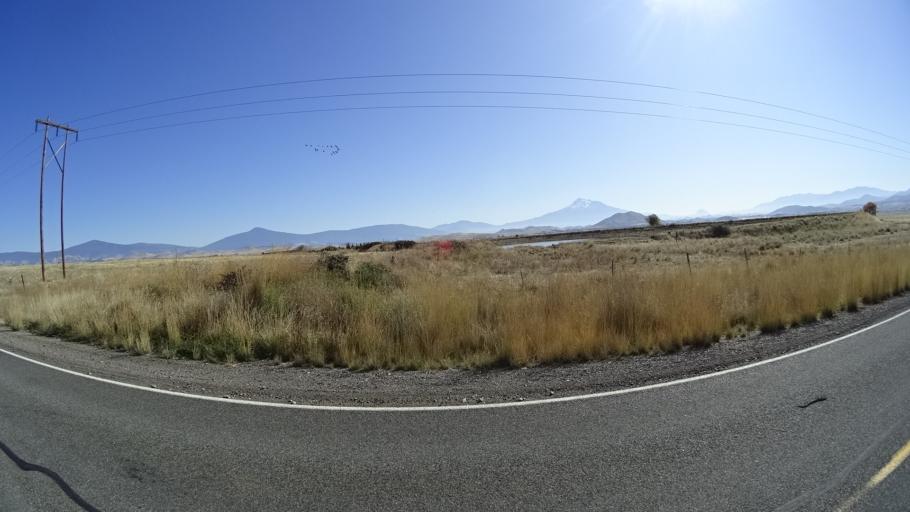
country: US
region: California
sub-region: Siskiyou County
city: Montague
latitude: 41.7654
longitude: -122.5559
